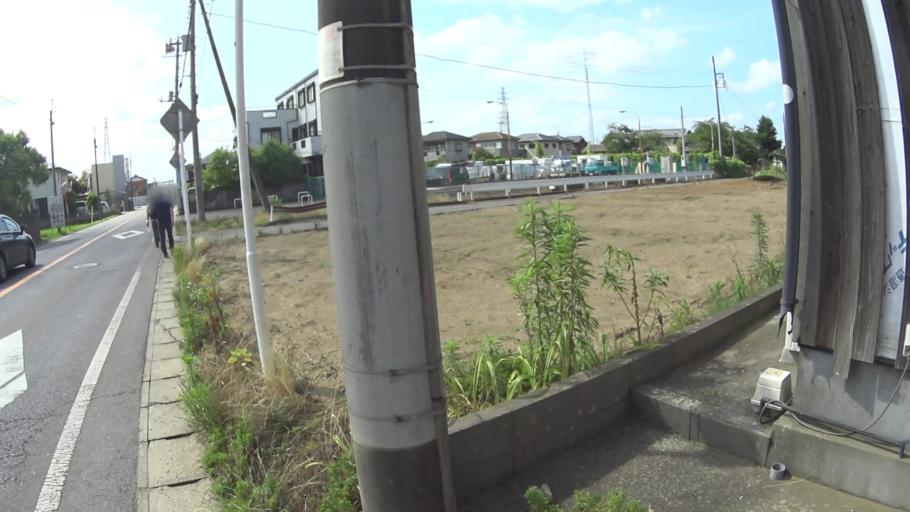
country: JP
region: Chiba
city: Sawara
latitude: 35.8862
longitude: 140.5144
